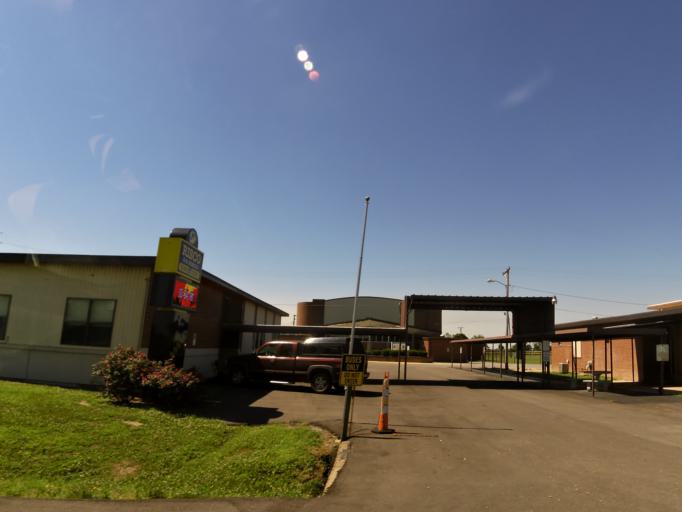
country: US
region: Missouri
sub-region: New Madrid County
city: Gideon
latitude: 36.5534
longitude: -89.8240
